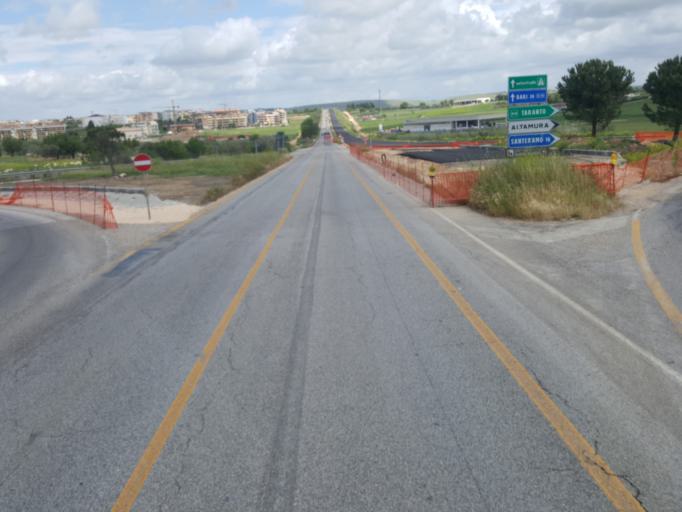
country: IT
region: Apulia
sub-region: Provincia di Bari
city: Altamura
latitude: 40.8246
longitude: 16.5706
